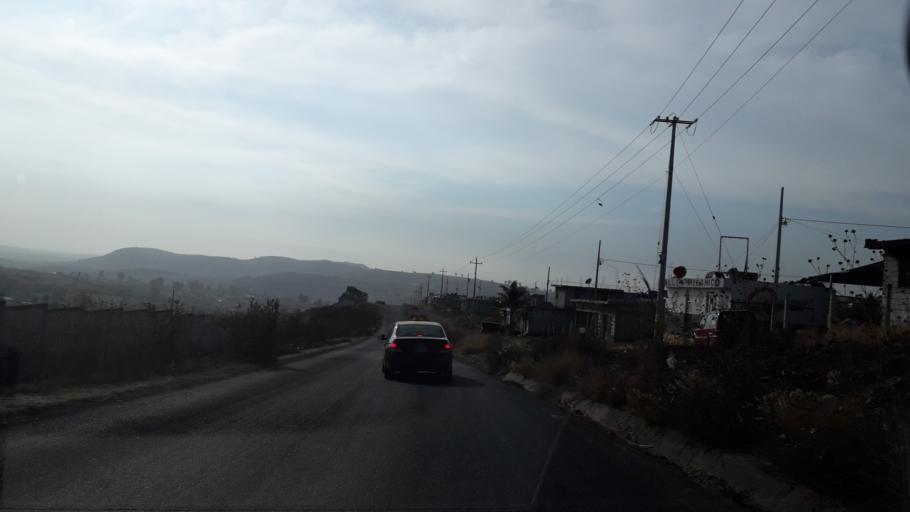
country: MX
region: Puebla
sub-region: Puebla
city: El Capulo (La Quebradora)
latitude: 18.9329
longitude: -98.2639
